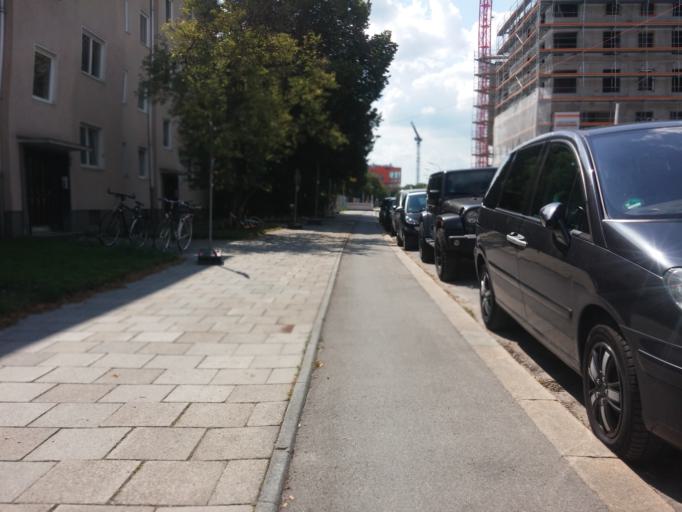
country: DE
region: Bavaria
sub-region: Upper Bavaria
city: Bogenhausen
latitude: 48.1246
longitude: 11.6125
